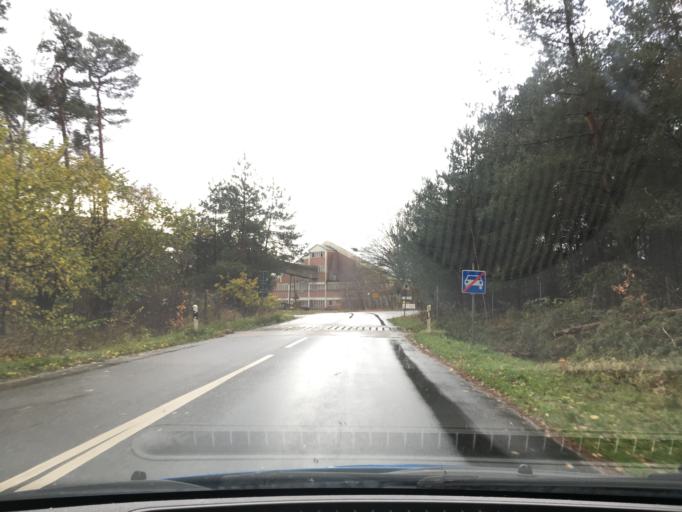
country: DE
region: Lower Saxony
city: Embsen
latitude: 53.1927
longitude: 10.3717
